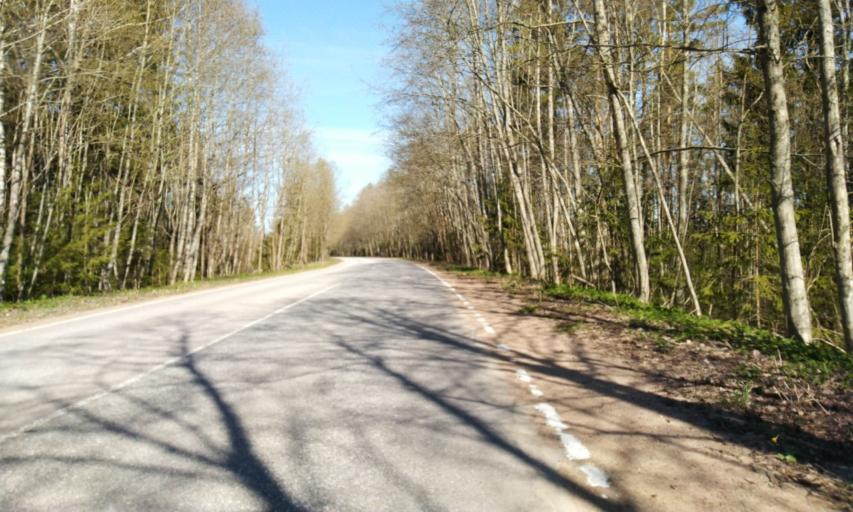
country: RU
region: Leningrad
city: Garbolovo
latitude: 60.4021
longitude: 30.4742
